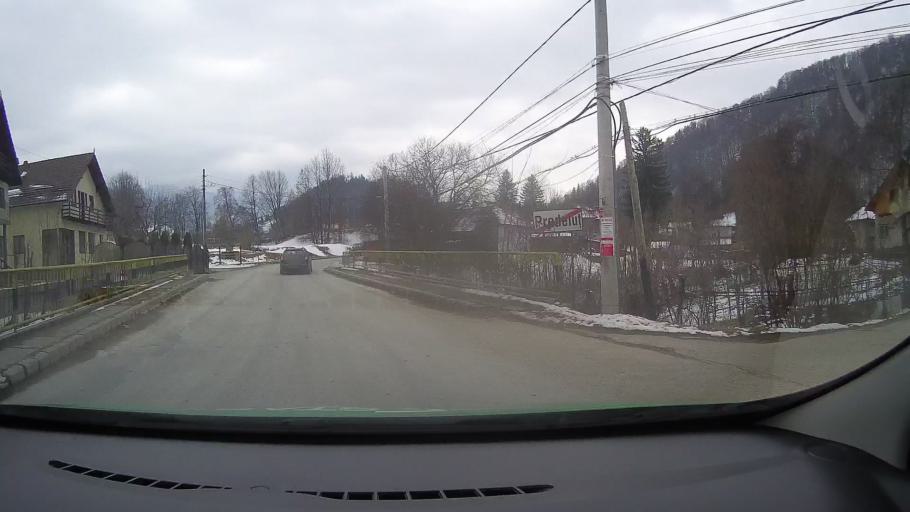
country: RO
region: Brasov
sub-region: Comuna Bran
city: Bran
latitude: 45.5210
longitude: 25.3660
